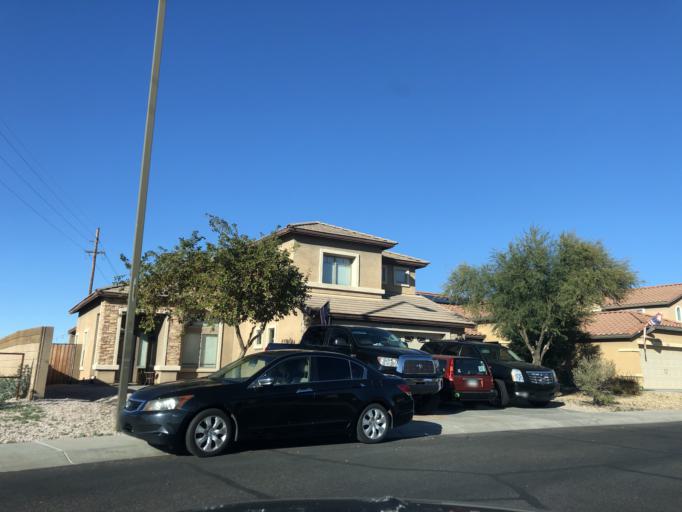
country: US
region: Arizona
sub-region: Maricopa County
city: Buckeye
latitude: 33.4269
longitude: -112.6079
